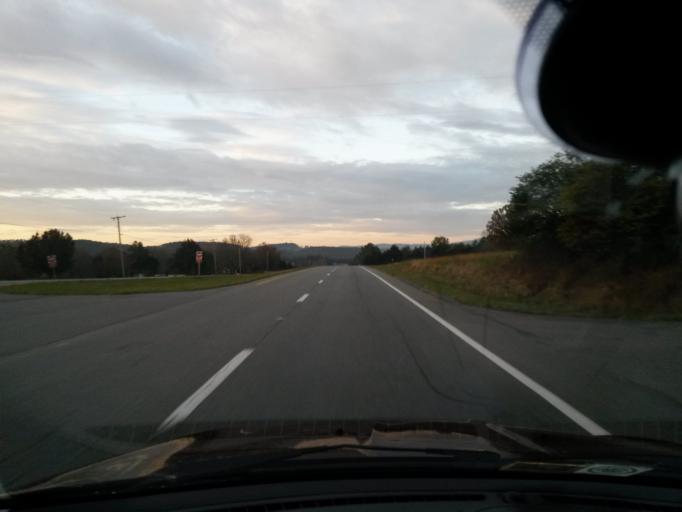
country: US
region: Virginia
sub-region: Botetourt County
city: Fincastle
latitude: 37.5309
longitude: -79.8711
